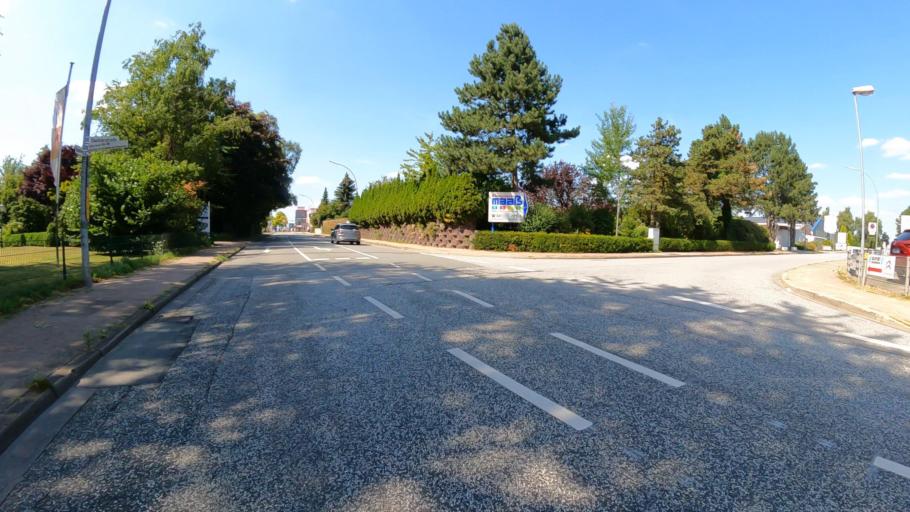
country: DE
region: Schleswig-Holstein
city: Kolln-Reisiek
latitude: 53.7418
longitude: 9.6904
